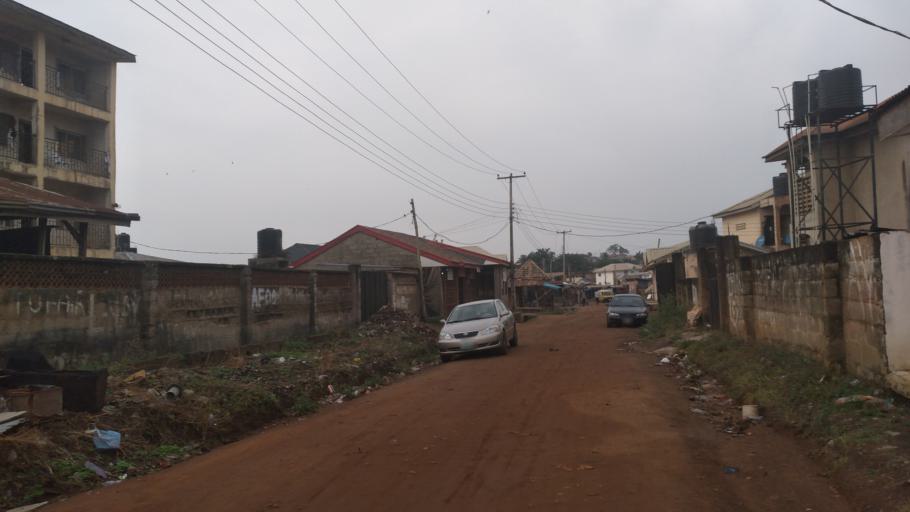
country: NG
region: Ondo
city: Akure
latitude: 7.2938
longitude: 5.1539
